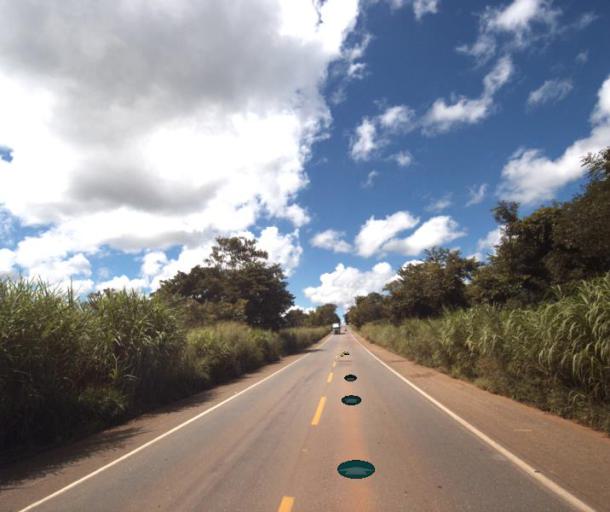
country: BR
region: Goias
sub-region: Petrolina De Goias
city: Petrolina de Goias
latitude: -15.9766
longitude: -49.1650
